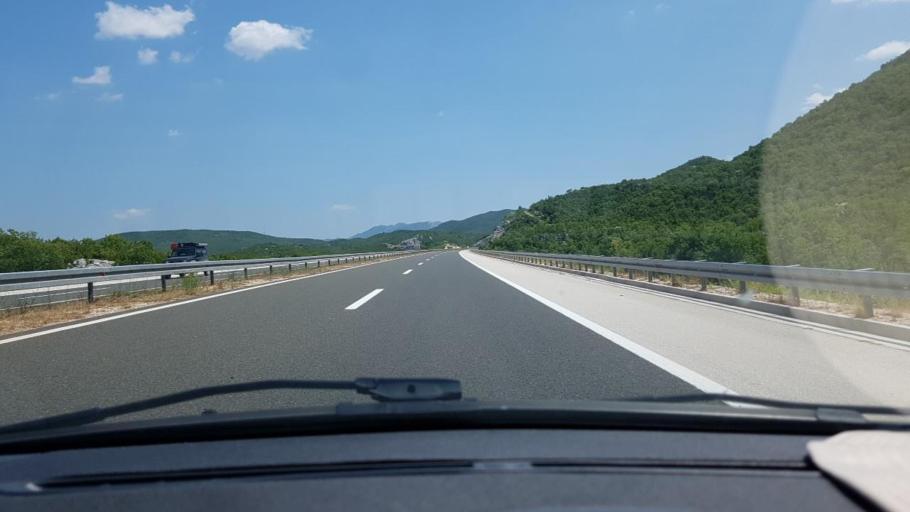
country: HR
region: Splitsko-Dalmatinska
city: Grubine
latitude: 43.3589
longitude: 17.1037
